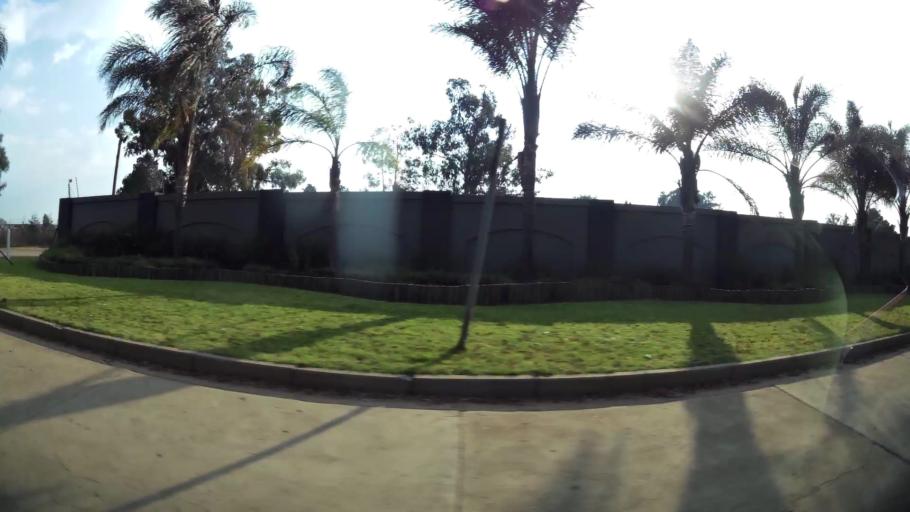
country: ZA
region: Gauteng
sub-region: Ekurhuleni Metropolitan Municipality
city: Benoni
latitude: -26.1102
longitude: 28.2748
